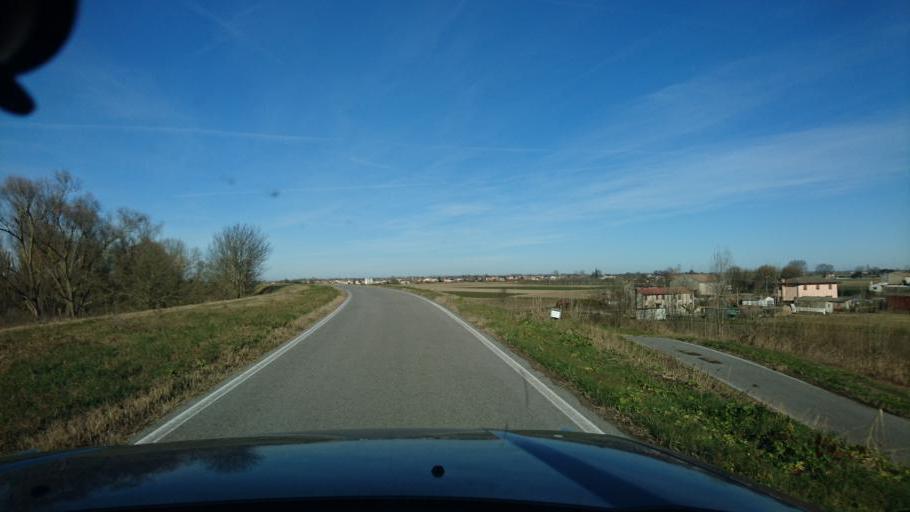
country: IT
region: Veneto
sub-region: Provincia di Rovigo
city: Corbola
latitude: 44.9857
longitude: 12.0888
